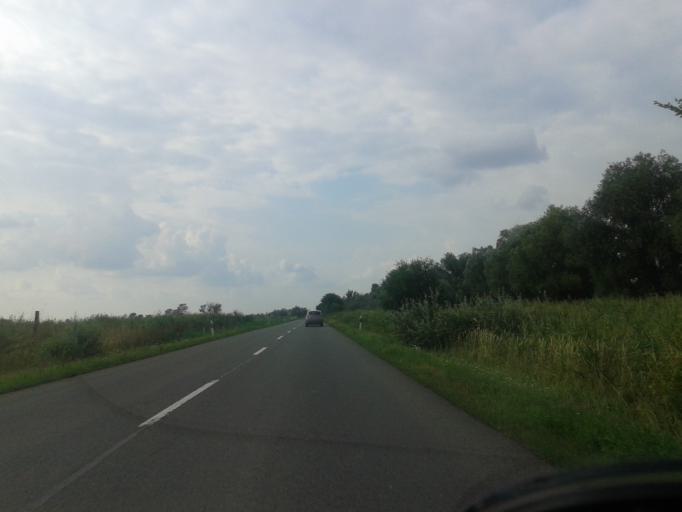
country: HU
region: Bacs-Kiskun
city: Akaszto
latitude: 46.7270
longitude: 19.1698
